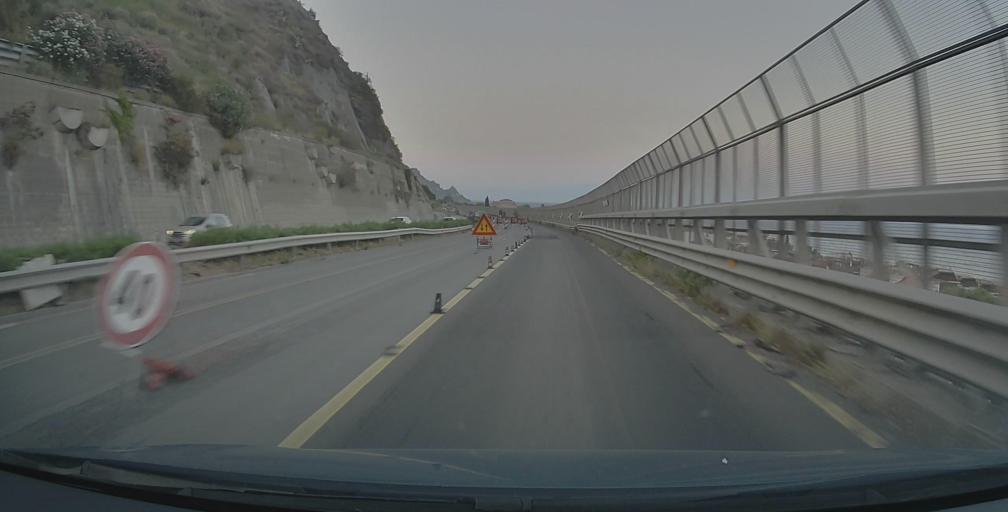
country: IT
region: Sicily
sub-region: Messina
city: Letojanni
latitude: 37.8887
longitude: 15.3151
